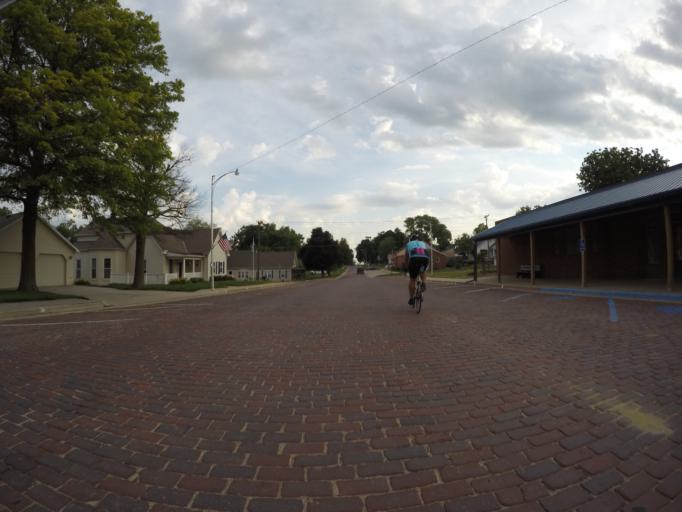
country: US
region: Kansas
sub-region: Doniphan County
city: Troy
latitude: 39.7873
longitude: -95.0897
